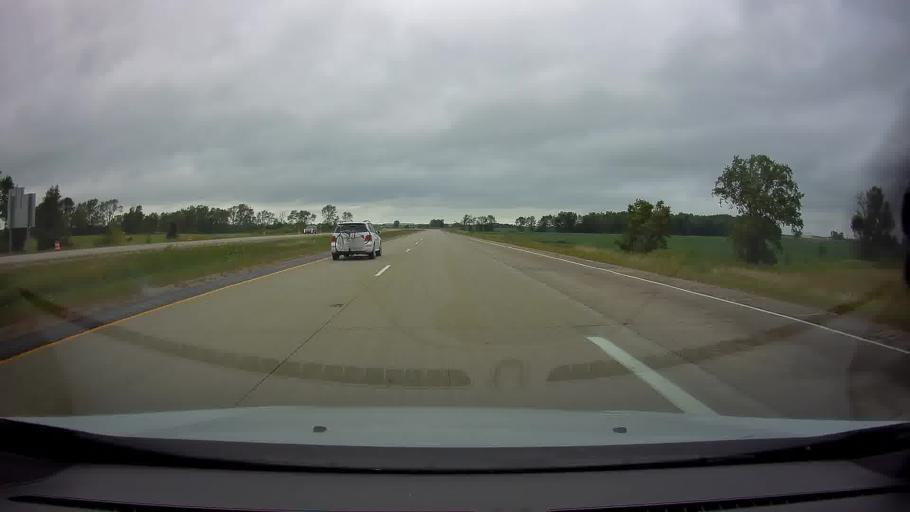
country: US
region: Wisconsin
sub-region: Brown County
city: Pulaski
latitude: 44.6785
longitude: -88.3106
